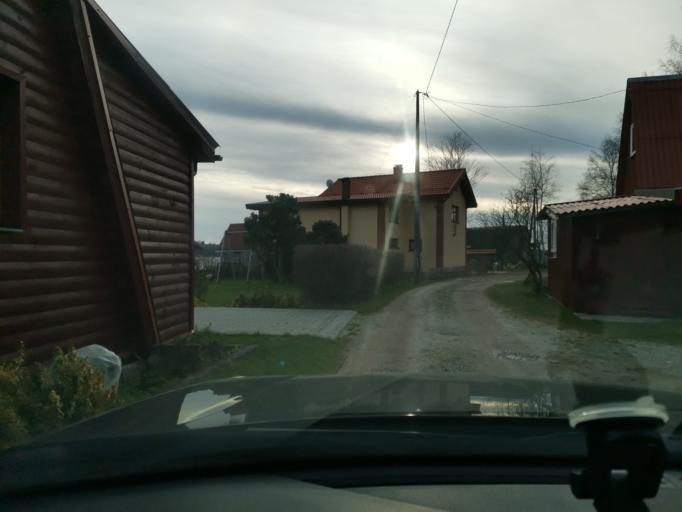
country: EE
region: Ida-Virumaa
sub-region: Sillamaee linn
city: Sillamae
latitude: 59.2537
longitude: 27.9173
